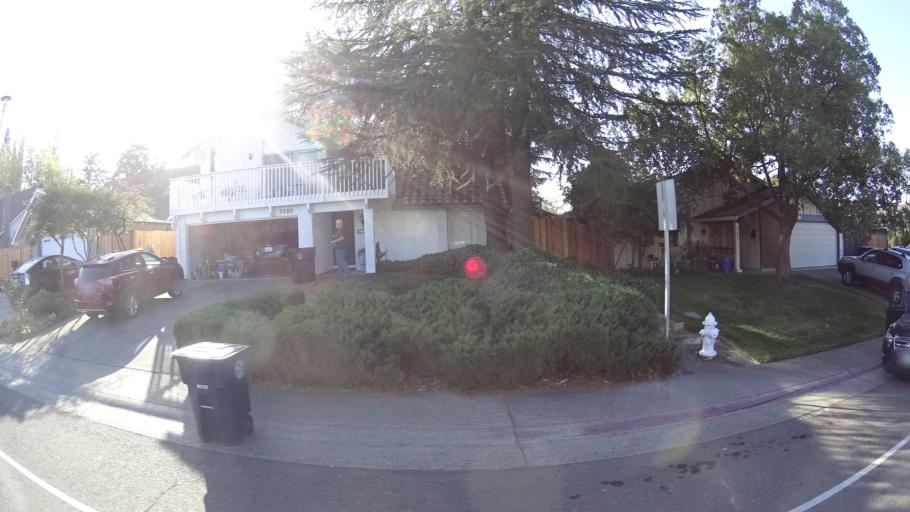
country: US
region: California
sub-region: Sacramento County
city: Citrus Heights
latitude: 38.6920
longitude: -121.2665
